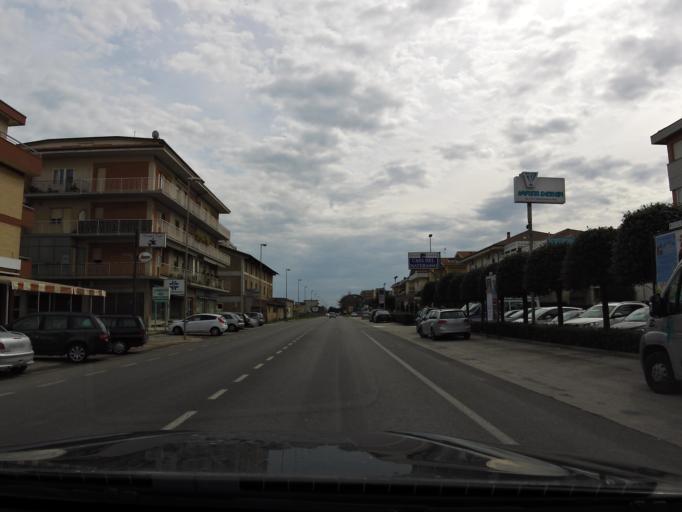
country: IT
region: The Marches
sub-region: Provincia di Macerata
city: Porto Potenza Picena
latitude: 43.3528
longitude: 13.7001
